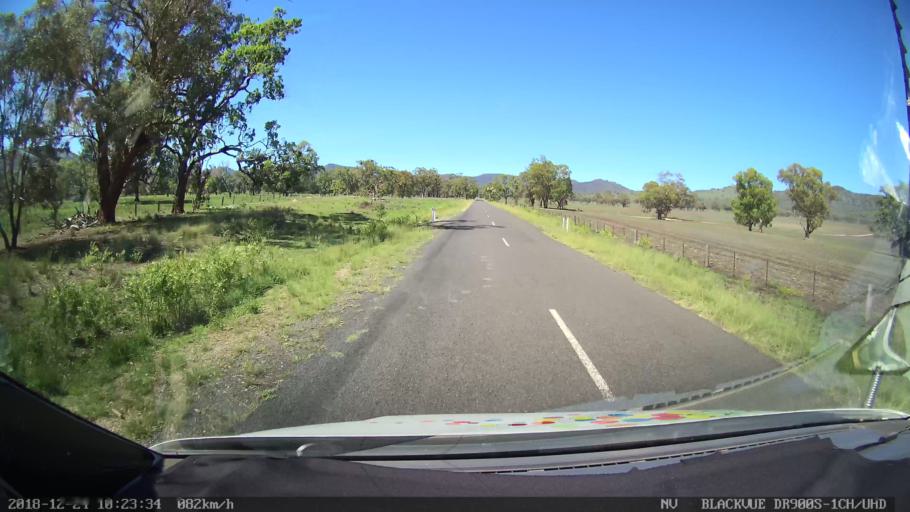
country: AU
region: New South Wales
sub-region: Liverpool Plains
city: Quirindi
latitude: -31.7766
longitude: 150.5370
